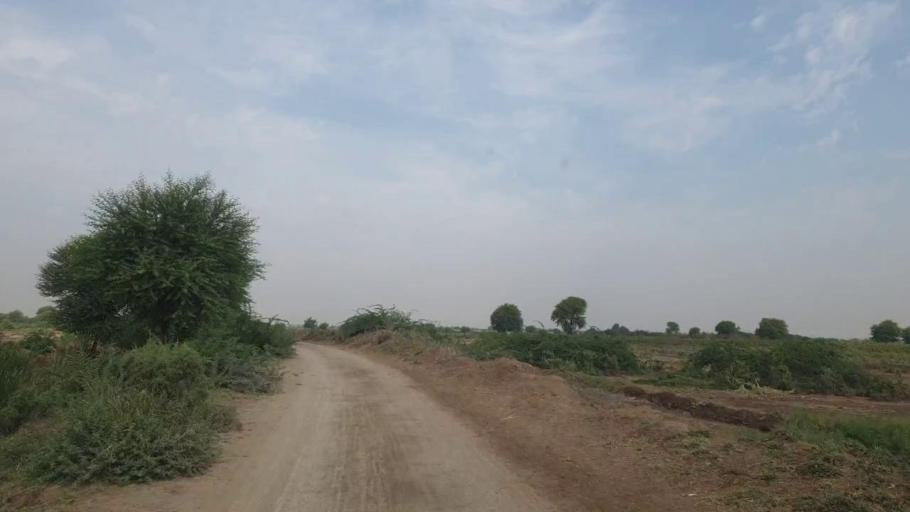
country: PK
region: Sindh
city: Rajo Khanani
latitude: 24.9695
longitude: 68.9968
